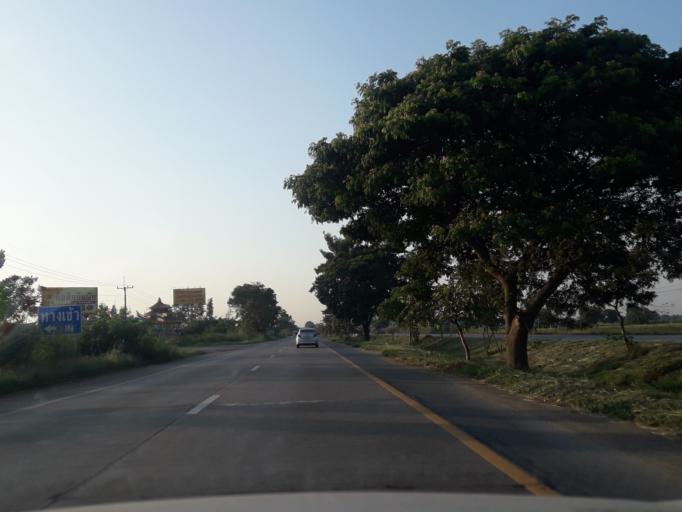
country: TH
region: Phra Nakhon Si Ayutthaya
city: Bang Pa-in
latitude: 14.2583
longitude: 100.5346
